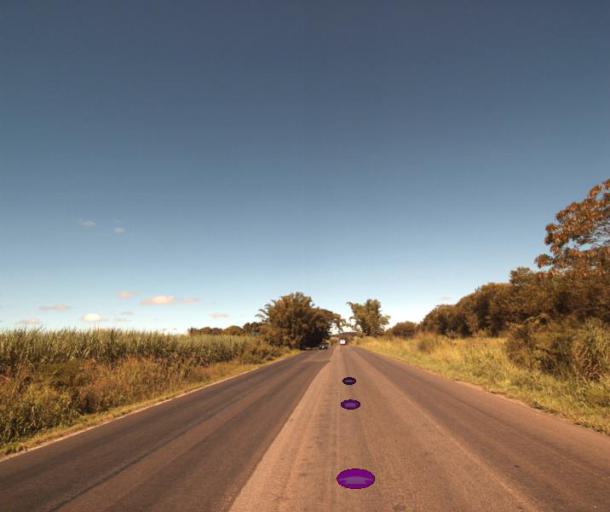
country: BR
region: Goias
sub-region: Itapaci
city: Itapaci
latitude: -15.1309
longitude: -49.5135
